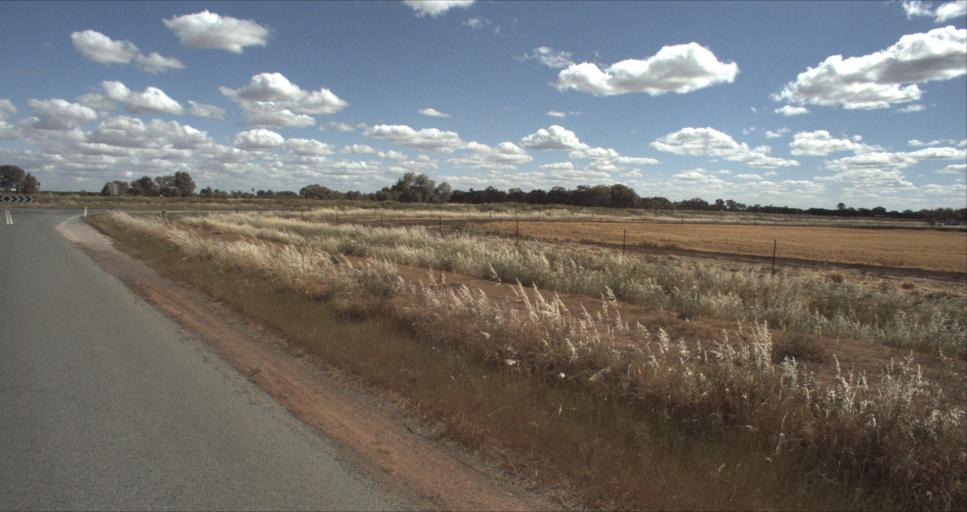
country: AU
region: New South Wales
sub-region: Leeton
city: Leeton
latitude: -34.5034
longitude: 146.2450
